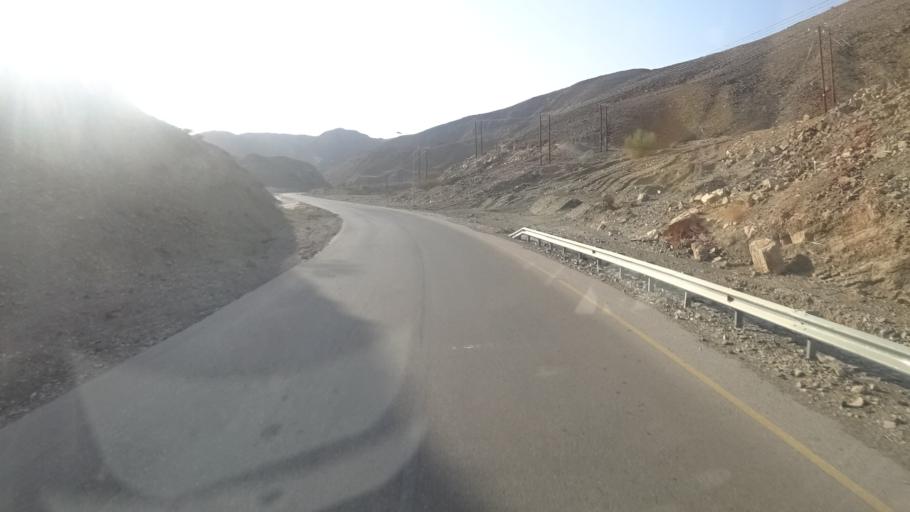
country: OM
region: Ash Sharqiyah
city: Badiyah
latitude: 22.5313
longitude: 58.9641
